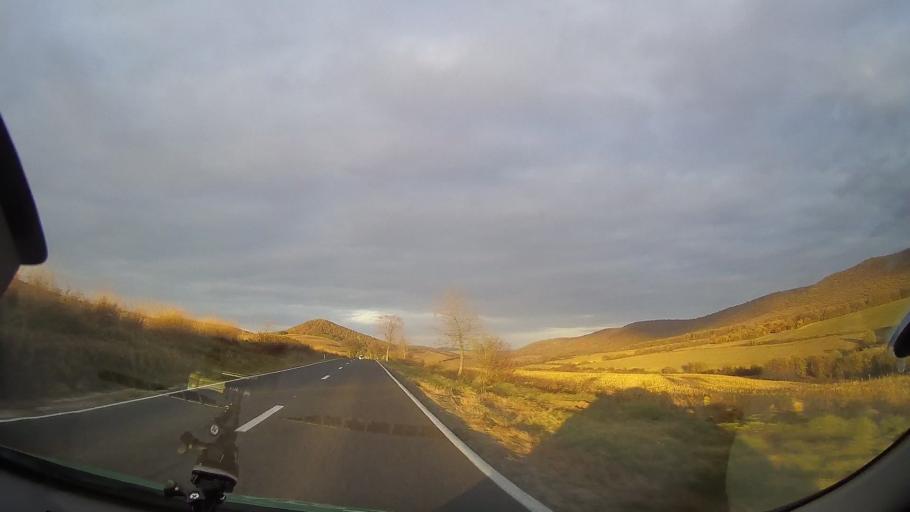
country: RO
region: Tulcea
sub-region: Comuna Ciucurova
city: Ciucurova
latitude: 44.9388
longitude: 28.4916
